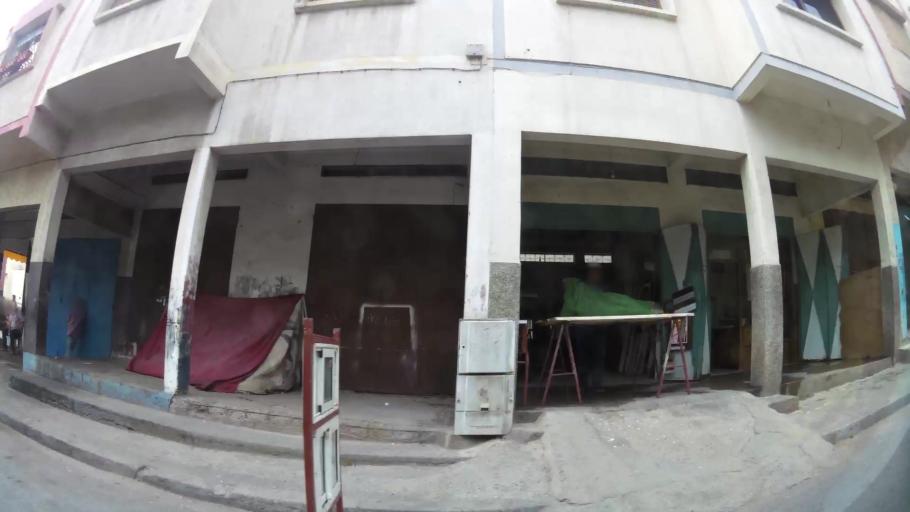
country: MA
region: Rabat-Sale-Zemmour-Zaer
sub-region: Rabat
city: Rabat
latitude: 33.9937
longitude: -6.8726
